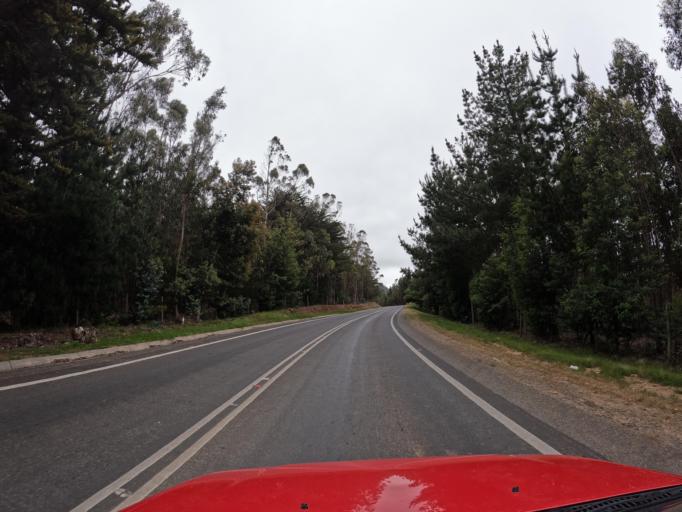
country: CL
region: O'Higgins
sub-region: Provincia de Colchagua
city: Santa Cruz
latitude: -34.5940
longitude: -72.0164
